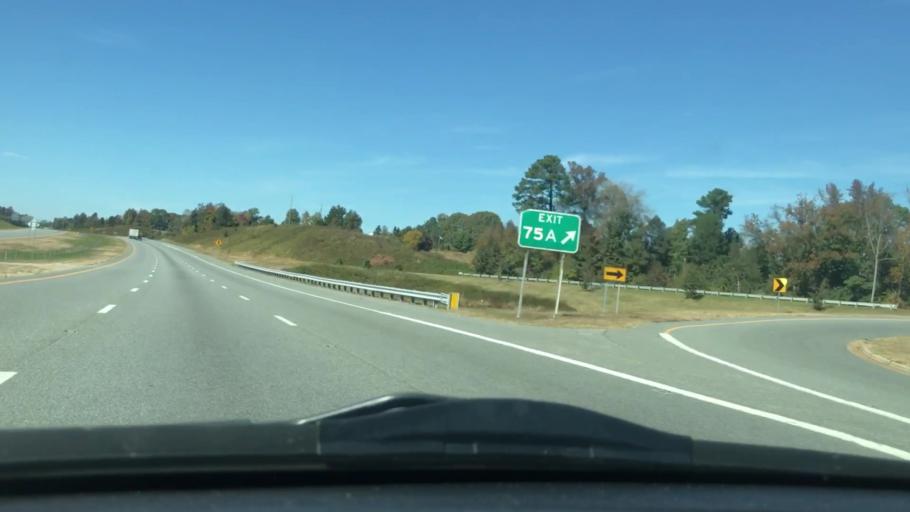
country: US
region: North Carolina
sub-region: Randolph County
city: Archdale
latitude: 35.9299
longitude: -79.9254
